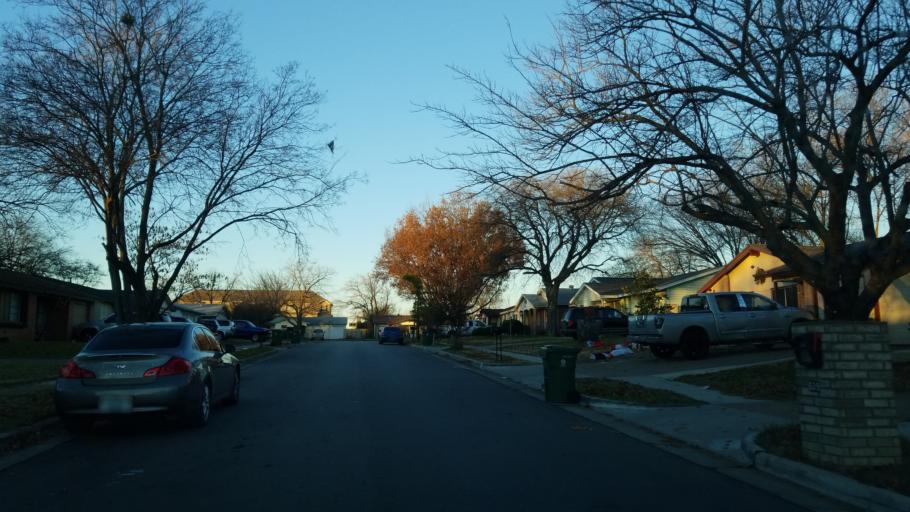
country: US
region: Texas
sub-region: Tarrant County
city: Arlington
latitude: 32.7312
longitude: -97.0572
